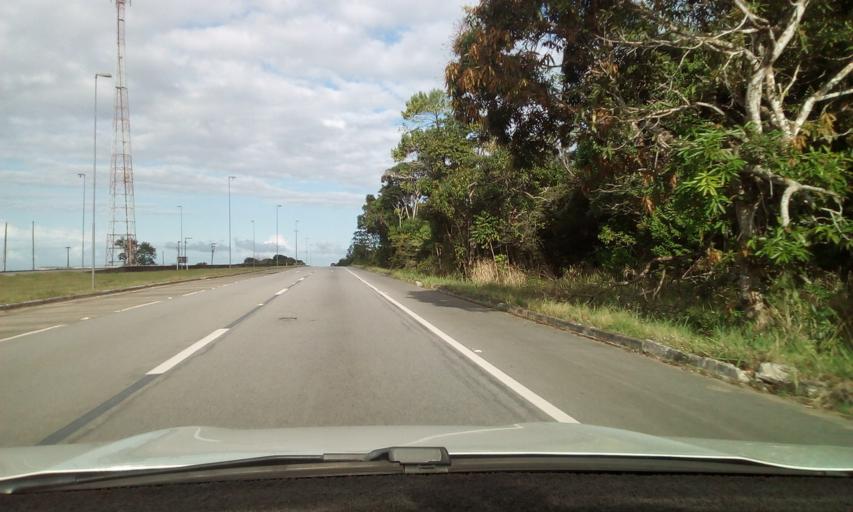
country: BR
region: Paraiba
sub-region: Santa Rita
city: Santa Rita
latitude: -7.0579
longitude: -35.0257
